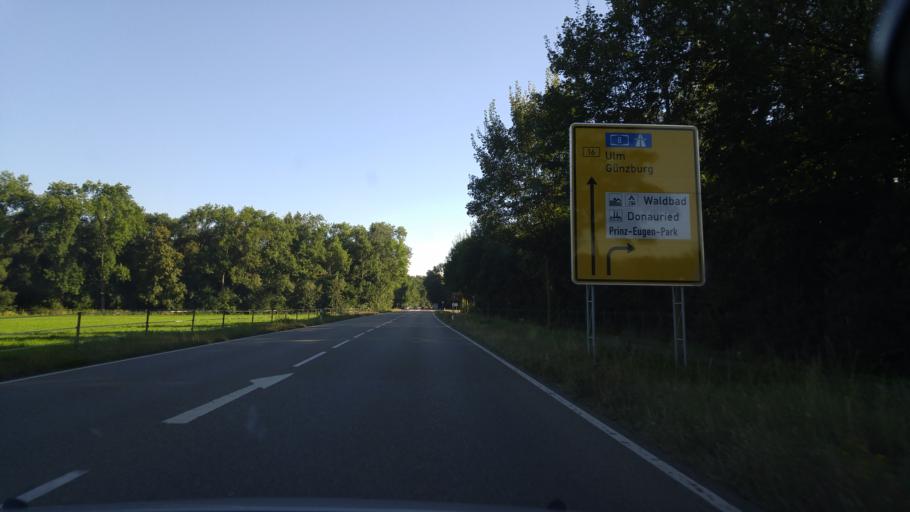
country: DE
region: Bavaria
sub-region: Swabia
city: Guenzburg
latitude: 48.4728
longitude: 10.2842
